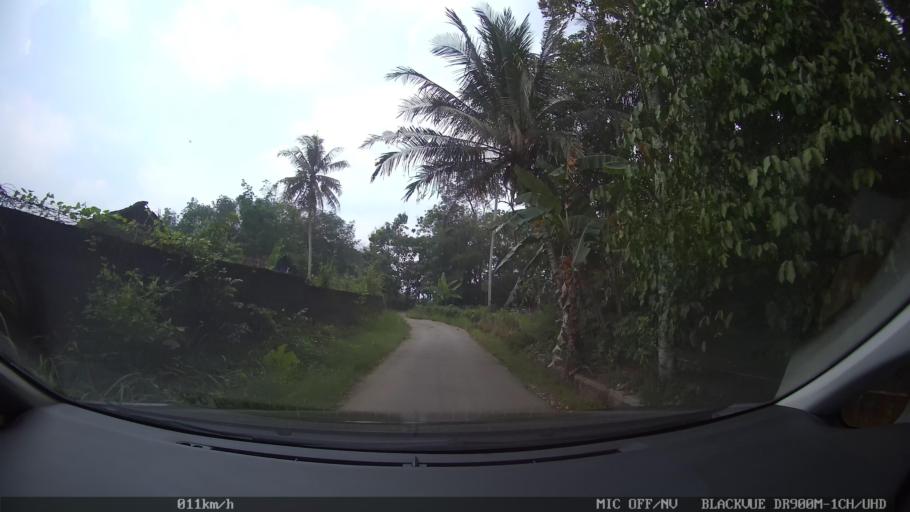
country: ID
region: Lampung
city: Gadingrejo
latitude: -5.3909
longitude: 105.0367
